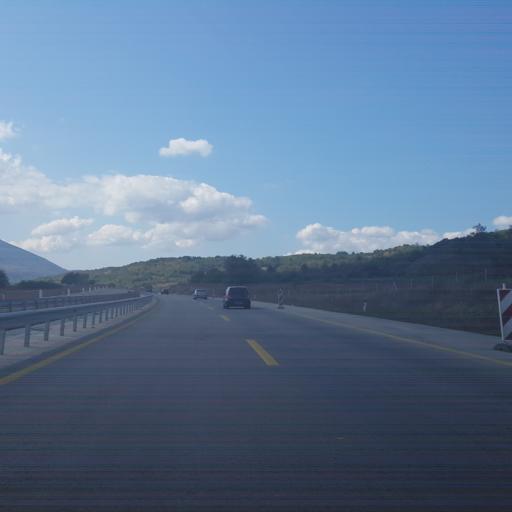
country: RS
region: Central Serbia
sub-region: Pirotski Okrug
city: Bela Palanka
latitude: 43.2367
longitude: 22.3466
